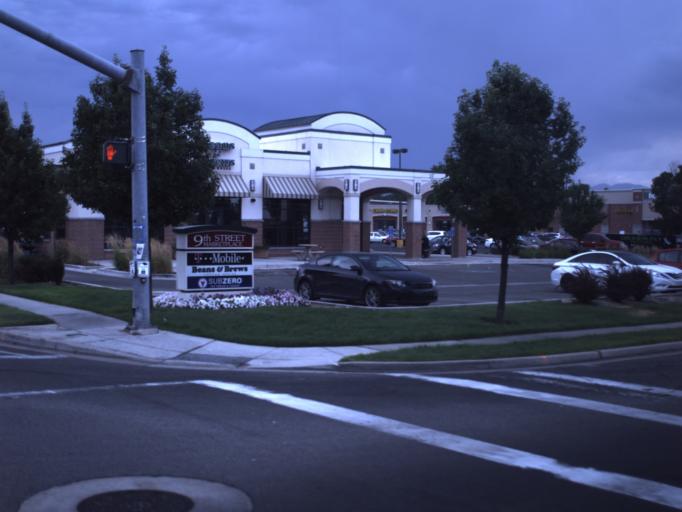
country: US
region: Utah
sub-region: Salt Lake County
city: Murray
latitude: 40.6496
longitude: -111.8660
